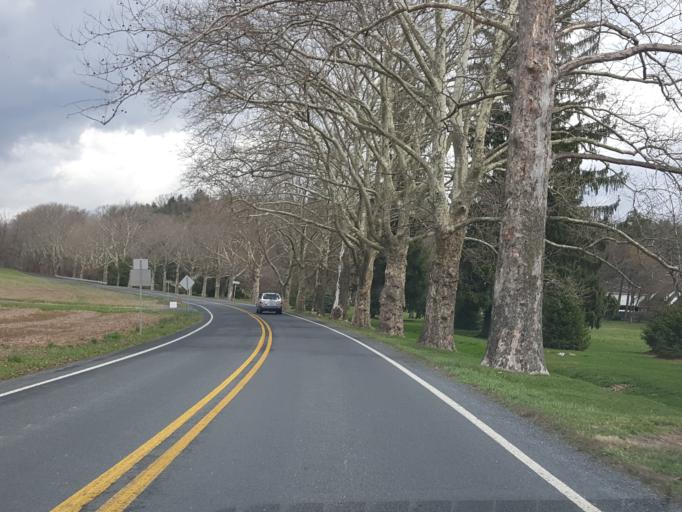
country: US
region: Pennsylvania
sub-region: Berks County
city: Robesonia
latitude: 40.3559
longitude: -76.1423
